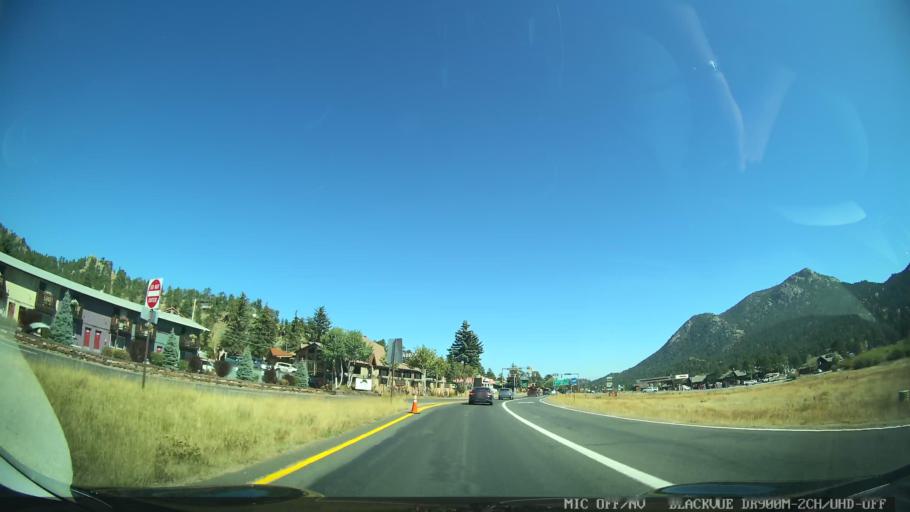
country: US
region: Colorado
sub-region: Larimer County
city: Estes Park
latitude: 40.3625
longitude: -105.5451
